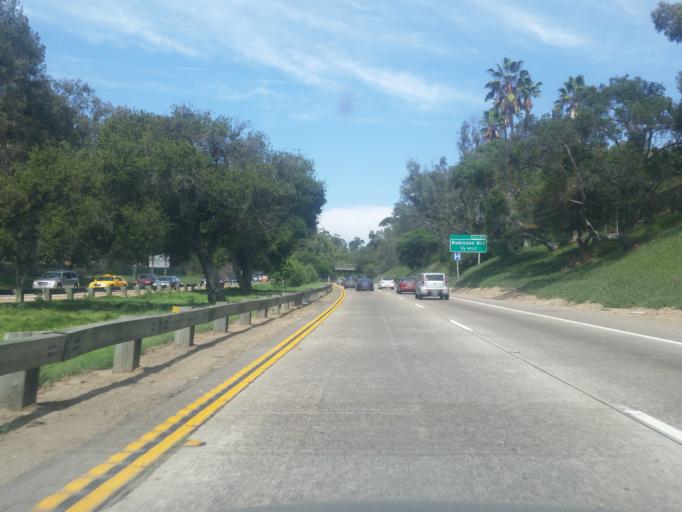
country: US
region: California
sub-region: San Diego County
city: San Diego
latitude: 32.7376
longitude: -117.1559
